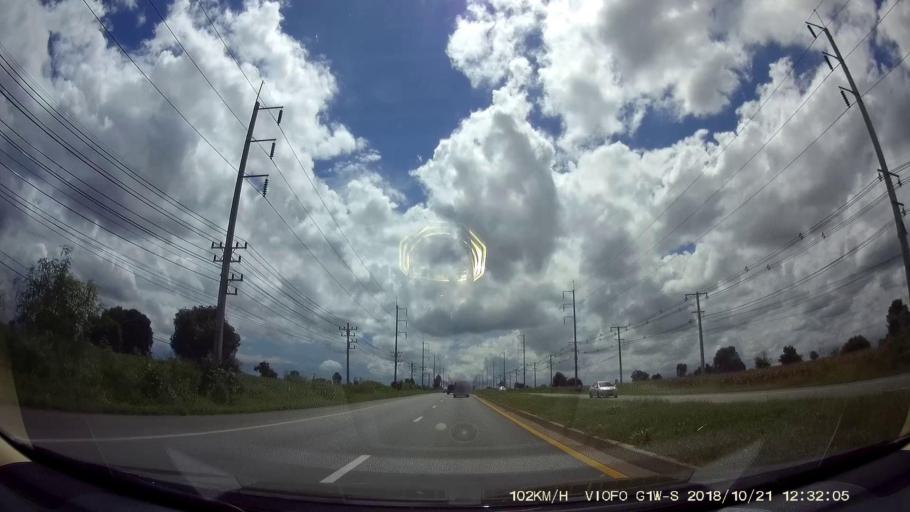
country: TH
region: Nakhon Ratchasima
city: Dan Khun Thot
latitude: 15.1466
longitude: 101.7320
